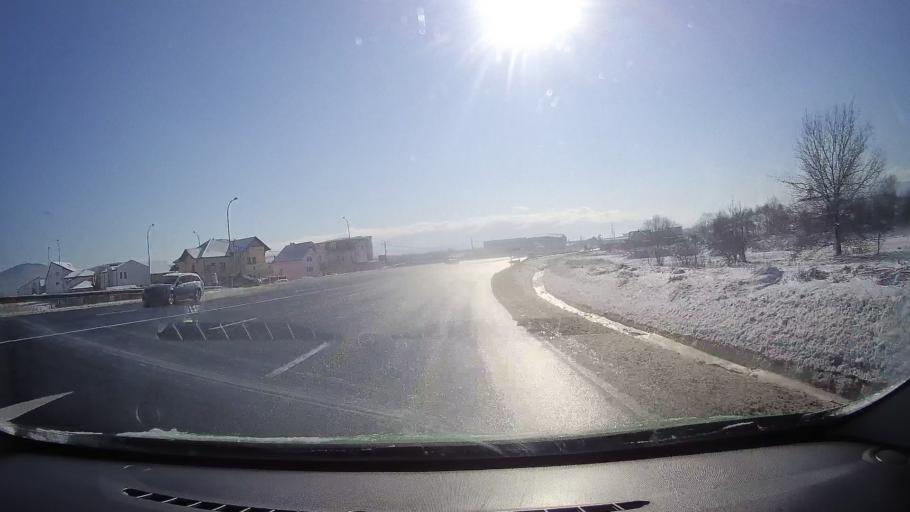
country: RO
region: Sibiu
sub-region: Comuna Selimbar
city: Selimbar
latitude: 45.7585
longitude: 24.1979
